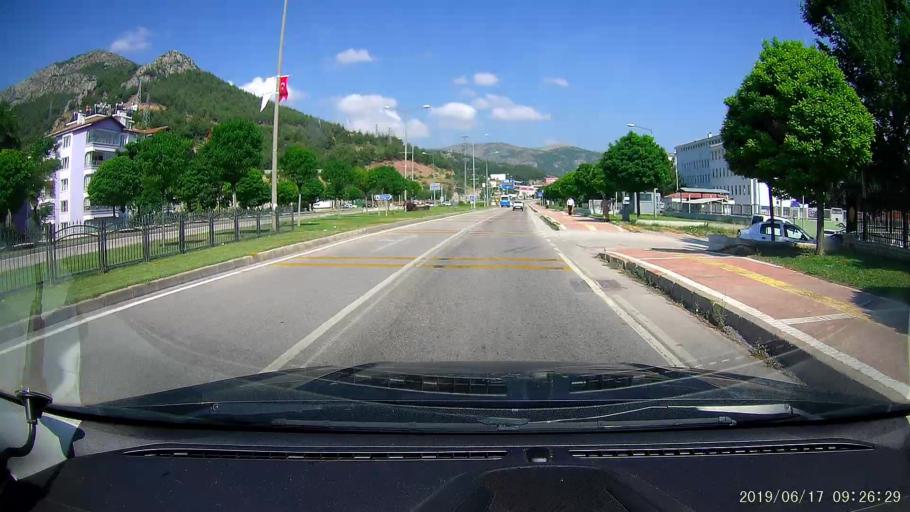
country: TR
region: Amasya
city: Amasya
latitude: 40.6697
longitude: 35.8351
